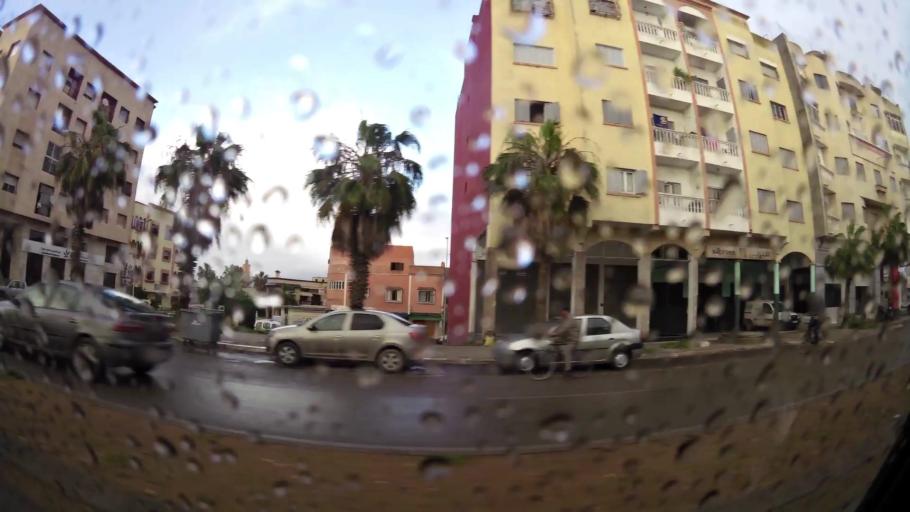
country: MA
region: Doukkala-Abda
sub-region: El-Jadida
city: El Jadida
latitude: 33.2276
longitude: -8.4935
